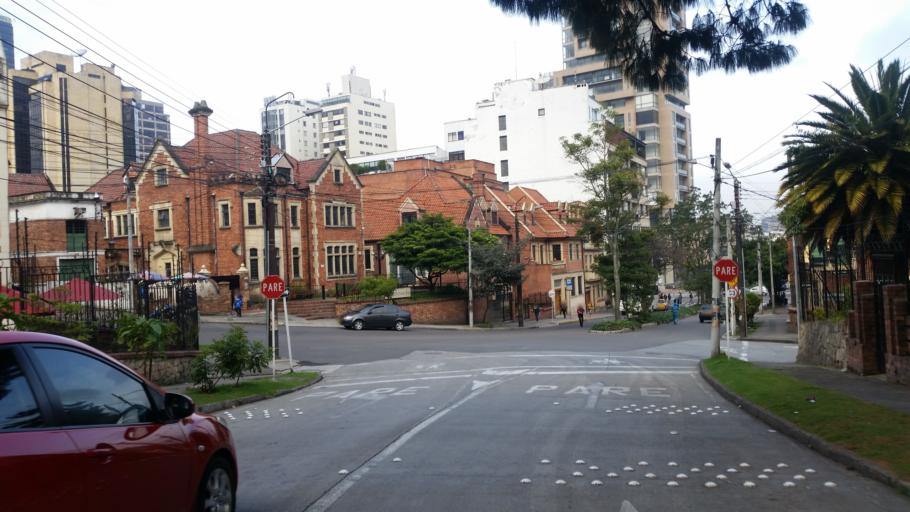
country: CO
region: Bogota D.C.
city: Bogota
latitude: 4.6211
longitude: -74.0659
